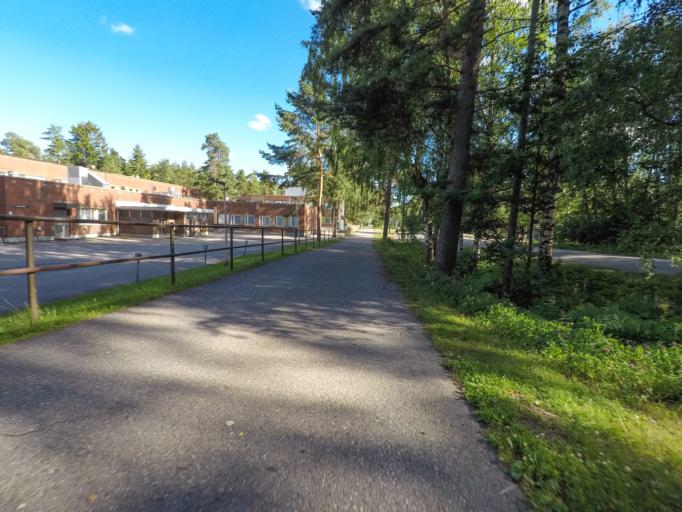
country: FI
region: South Karelia
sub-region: Lappeenranta
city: Lappeenranta
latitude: 61.0821
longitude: 28.1485
